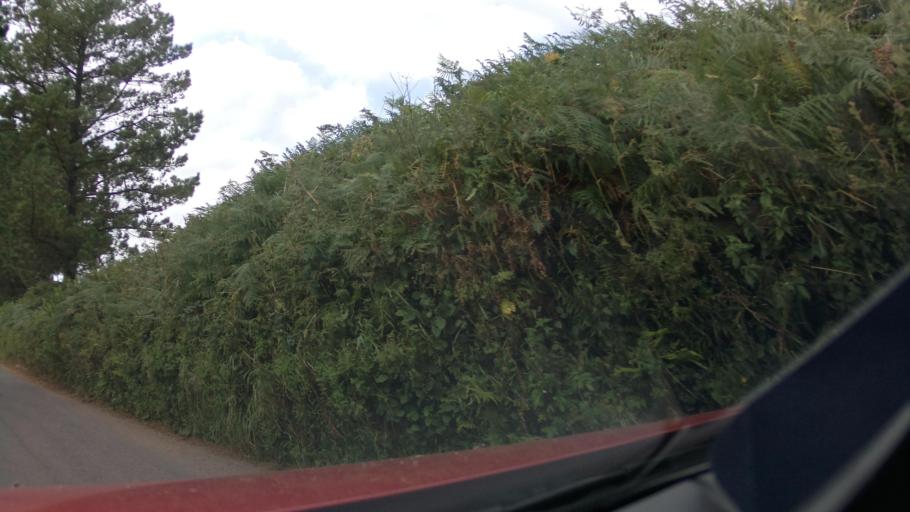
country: GB
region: England
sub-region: Devon
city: South Brent
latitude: 50.3982
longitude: -3.8351
